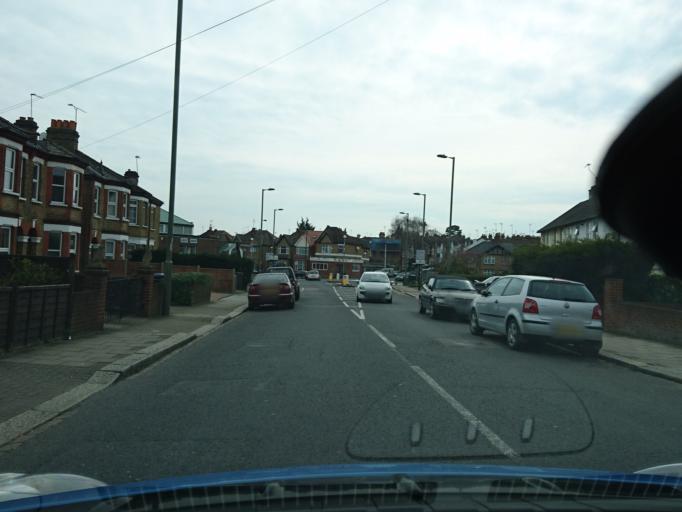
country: GB
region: England
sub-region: Greater London
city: Hadley Wood
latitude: 51.6442
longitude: -0.1657
